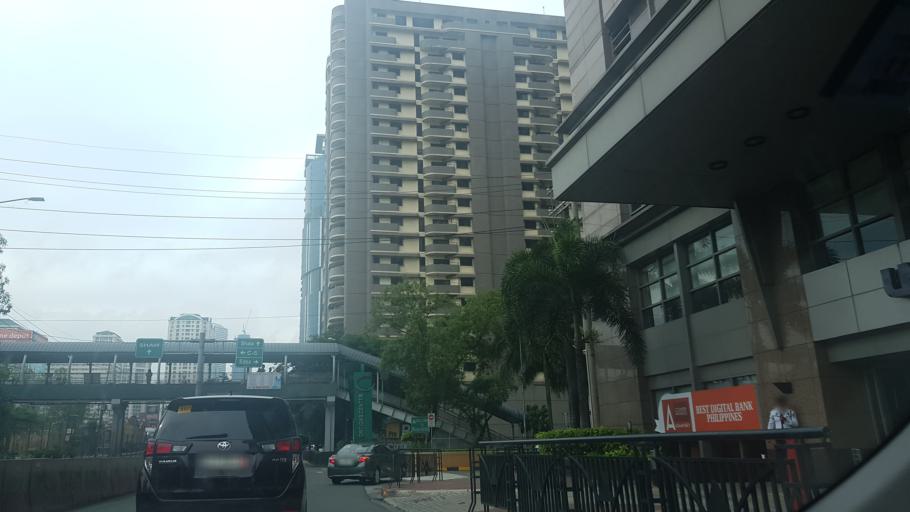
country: PH
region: Metro Manila
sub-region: Pasig
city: Pasig City
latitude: 14.5872
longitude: 121.0638
